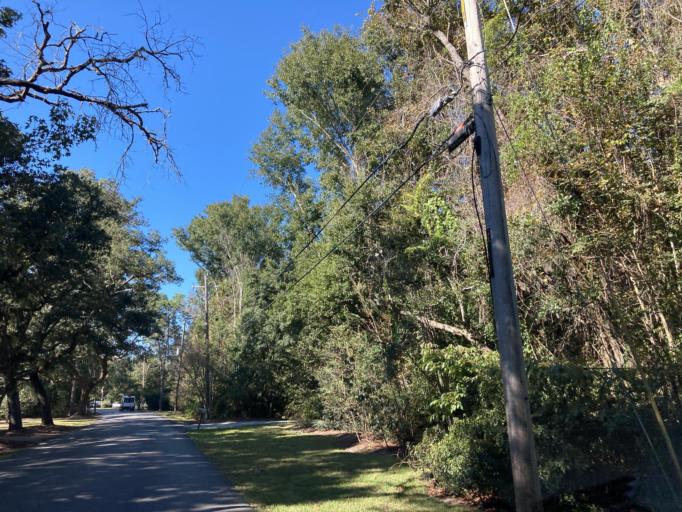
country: US
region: Mississippi
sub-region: Jackson County
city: Ocean Springs
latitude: 30.4028
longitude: -88.8172
